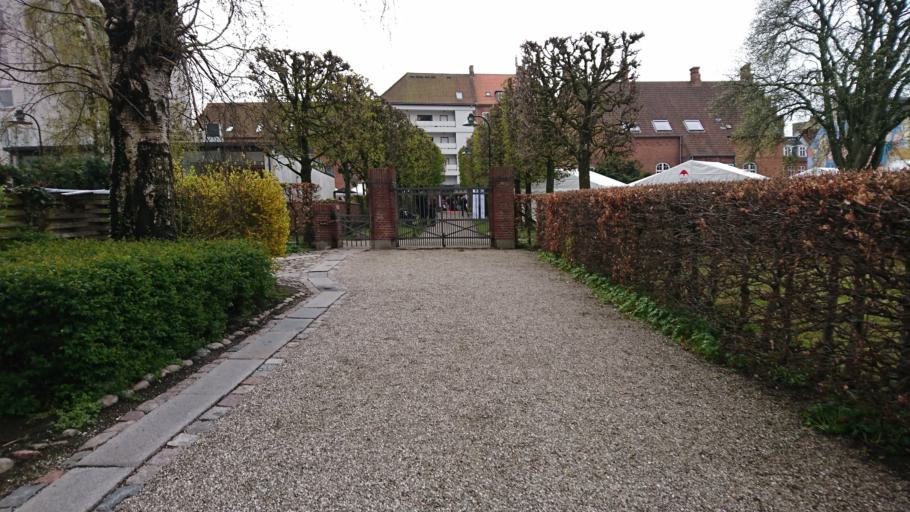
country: DK
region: Zealand
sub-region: Roskilde Kommune
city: Roskilde
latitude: 55.6416
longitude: 12.0865
